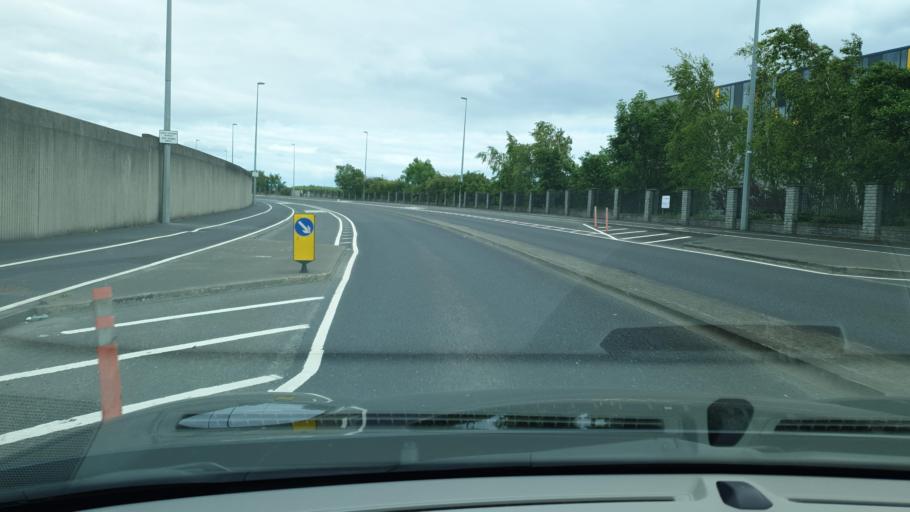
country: IE
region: Leinster
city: Lucan
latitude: 53.3369
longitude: -6.4257
